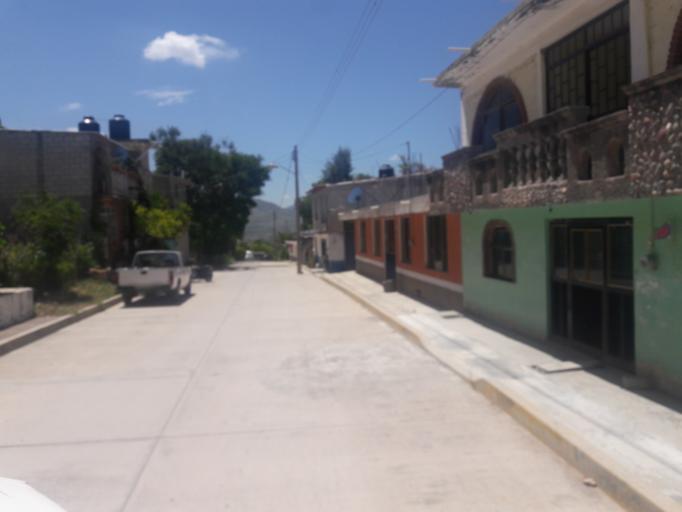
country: MX
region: Oaxaca
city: Ciudad de Huajuapam de Leon
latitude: 17.8038
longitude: -97.8007
